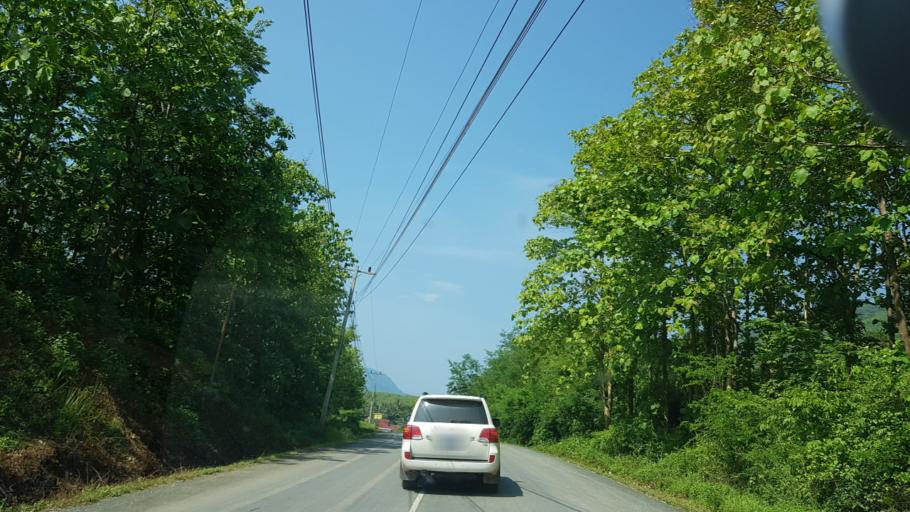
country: LA
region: Louangphabang
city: Xiang Ngeun
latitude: 19.7356
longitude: 102.1572
